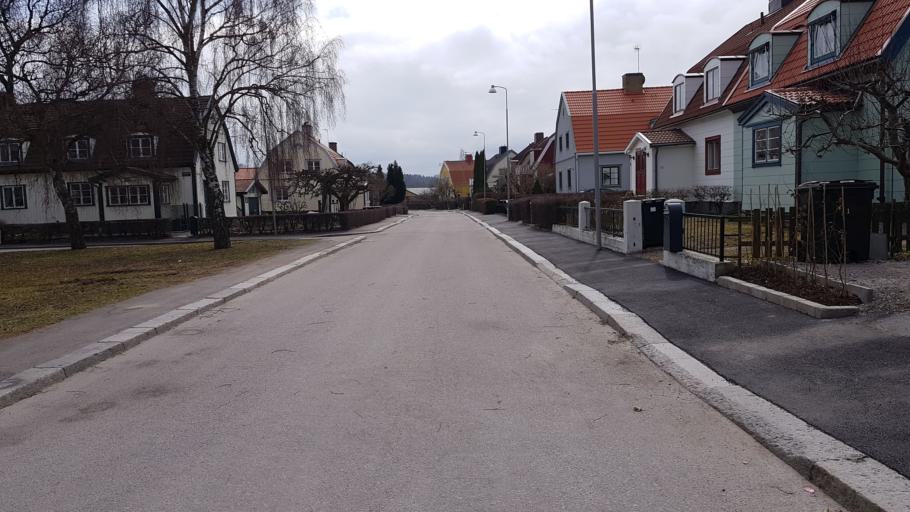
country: SE
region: OEstergoetland
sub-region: Norrkopings Kommun
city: Norrkoping
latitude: 58.5865
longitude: 16.2124
